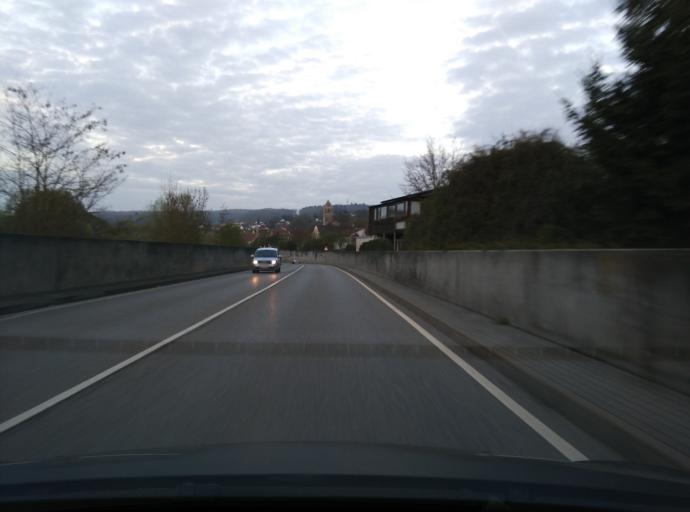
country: DE
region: Baden-Wuerttemberg
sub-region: Regierungsbezirk Stuttgart
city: Neckartailfingen
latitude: 48.6135
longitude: 9.2701
